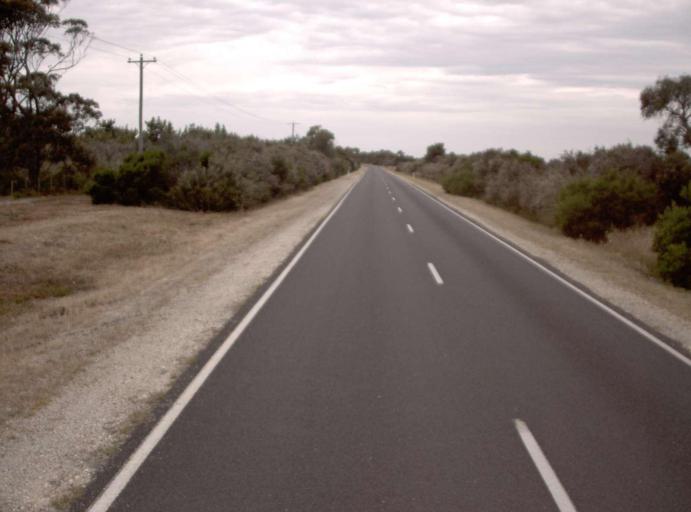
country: AU
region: Victoria
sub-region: Wellington
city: Sale
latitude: -38.1989
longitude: 147.3470
